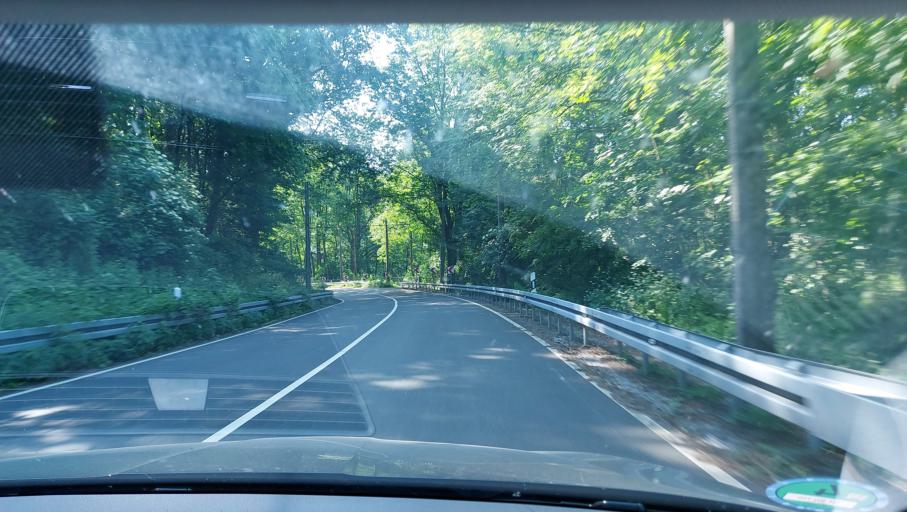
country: DE
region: North Rhine-Westphalia
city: Burscheid
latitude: 51.1359
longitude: 7.1381
